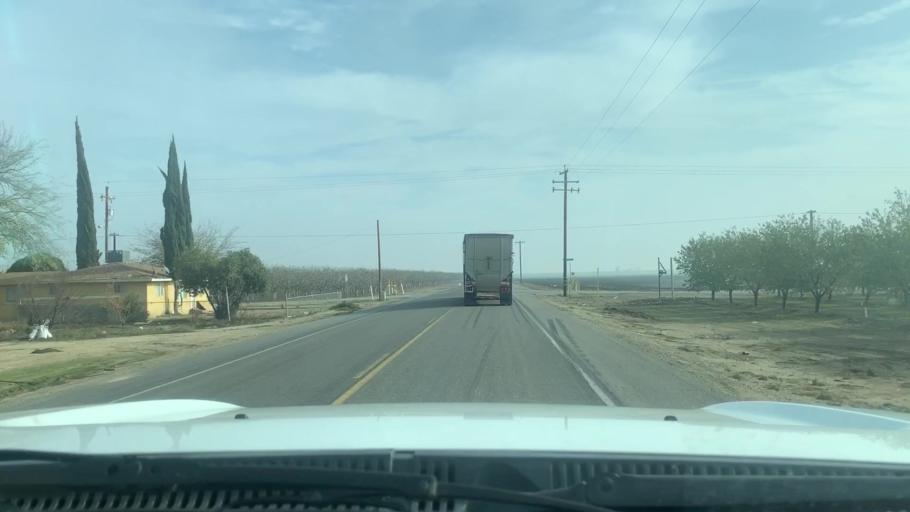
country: US
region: California
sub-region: Kern County
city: Shafter
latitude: 35.5001
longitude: -119.3687
